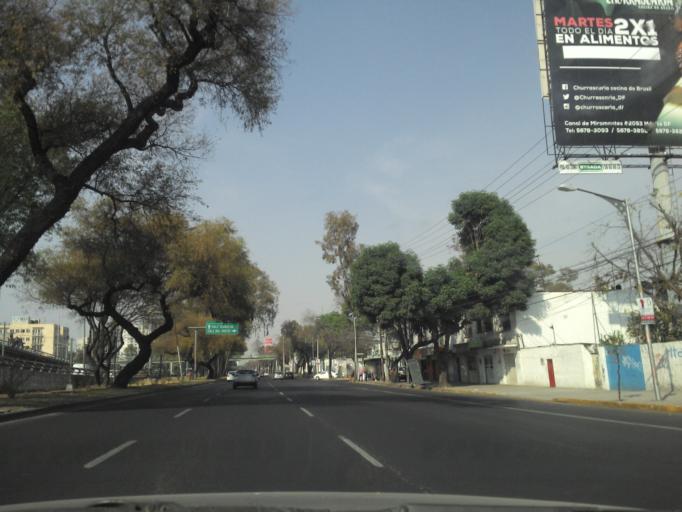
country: MX
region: Mexico City
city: Tlalpan
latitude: 19.3088
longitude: -99.1416
